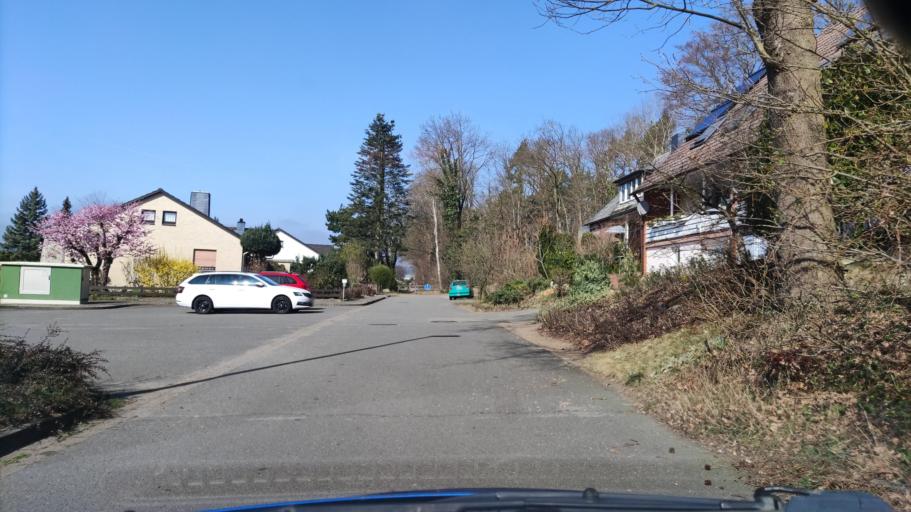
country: DE
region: Lower Saxony
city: Clenze
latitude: 52.9408
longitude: 10.9591
